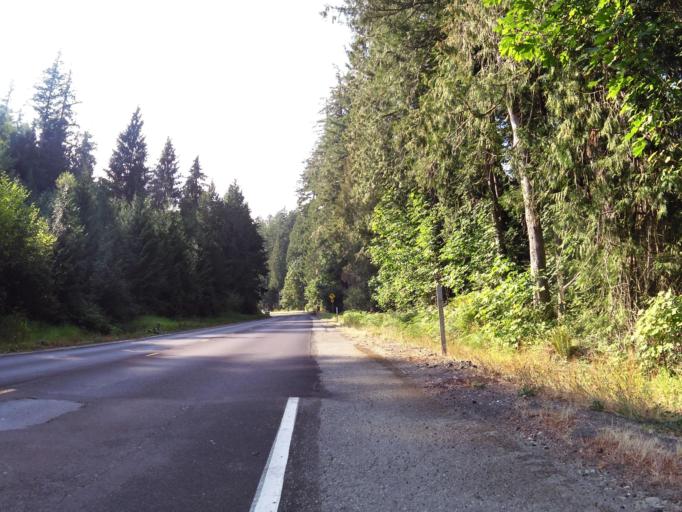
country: US
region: Washington
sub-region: Kitsap County
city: Erlands Point-Kitsap Lake
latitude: 47.5247
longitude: -122.7493
